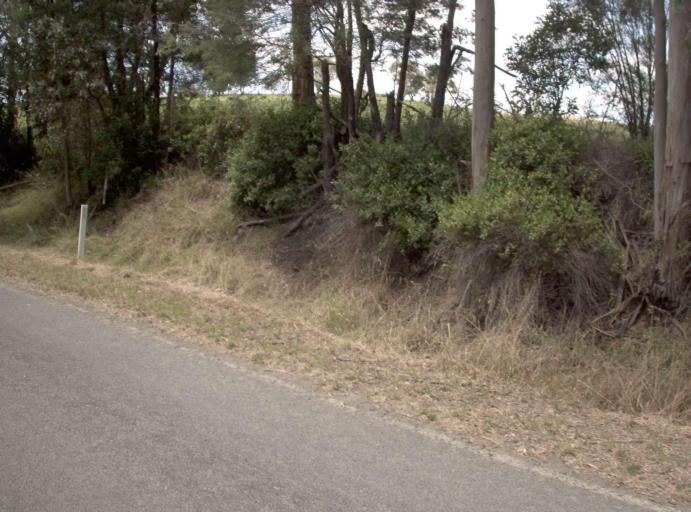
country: AU
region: Victoria
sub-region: Baw Baw
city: Warragul
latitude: -38.4901
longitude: 145.9959
